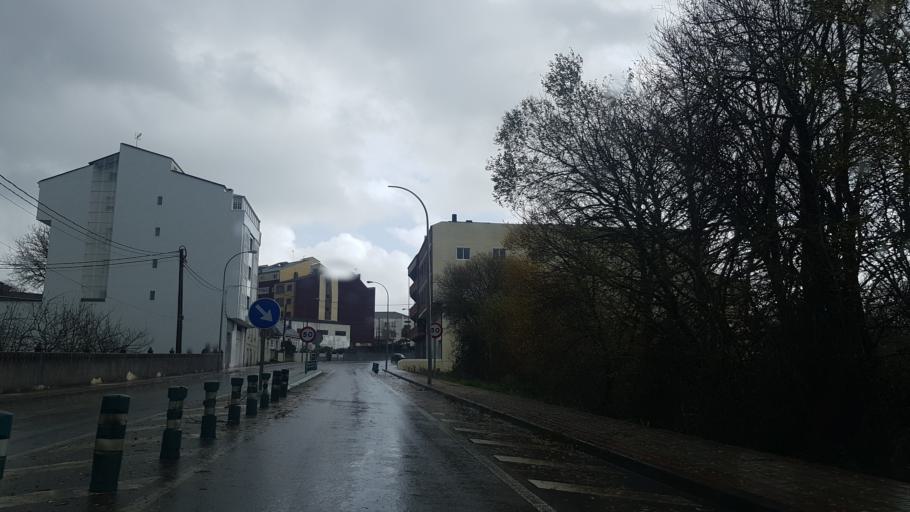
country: ES
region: Galicia
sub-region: Provincia de Lugo
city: Vilalba
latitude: 43.3040
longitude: -7.6838
